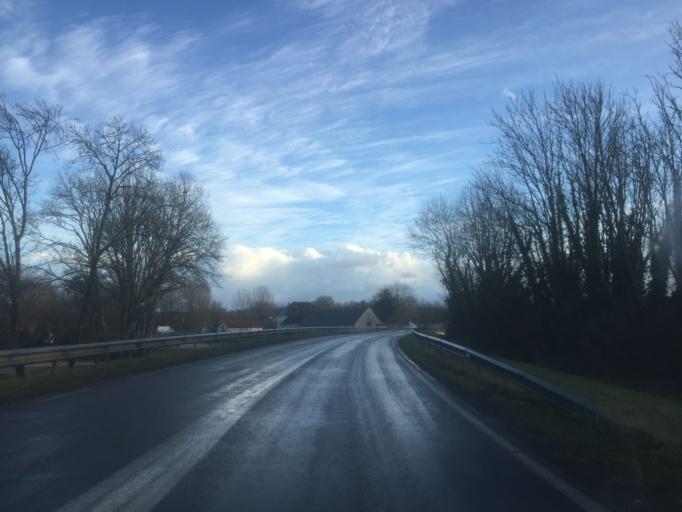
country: FR
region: Franche-Comte
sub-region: Departement du Jura
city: Dampierre
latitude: 47.1493
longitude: 5.7219
